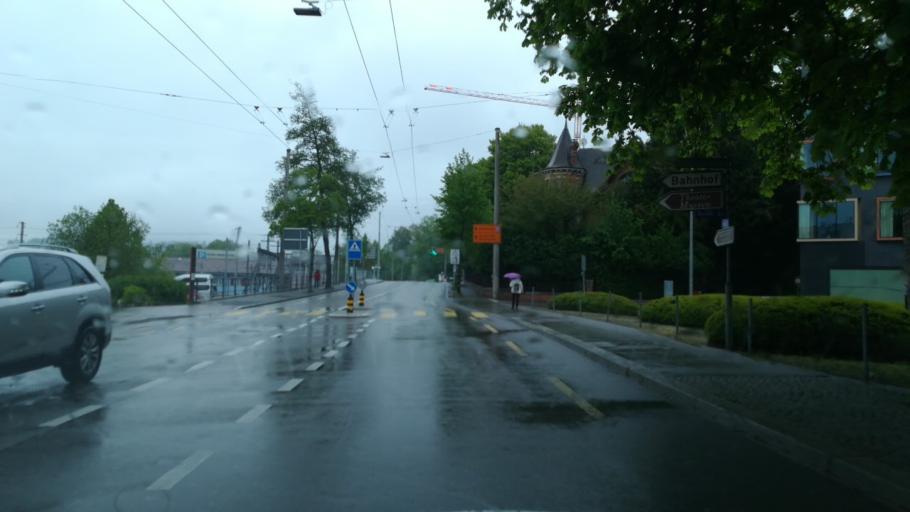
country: CH
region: Zurich
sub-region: Bezirk Winterthur
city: Stadt Winterthur (Kreis 1) / Lind
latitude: 47.5043
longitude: 8.7296
